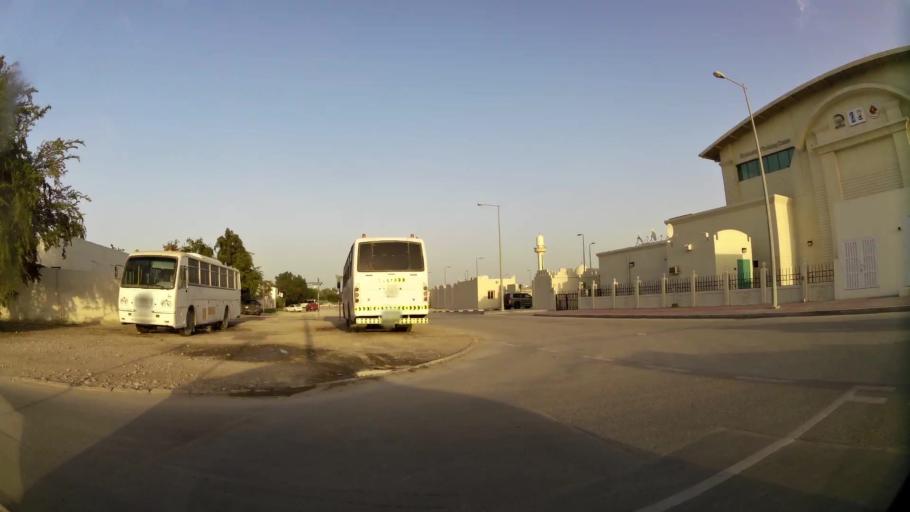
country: QA
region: Baladiyat ar Rayyan
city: Ar Rayyan
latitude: 25.3162
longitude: 51.4582
